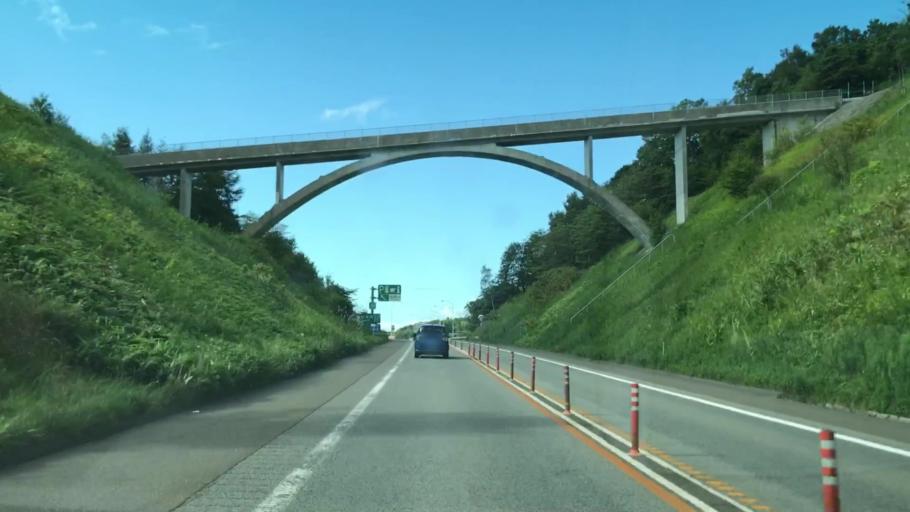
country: JP
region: Hokkaido
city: Date
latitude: 42.4612
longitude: 140.9110
